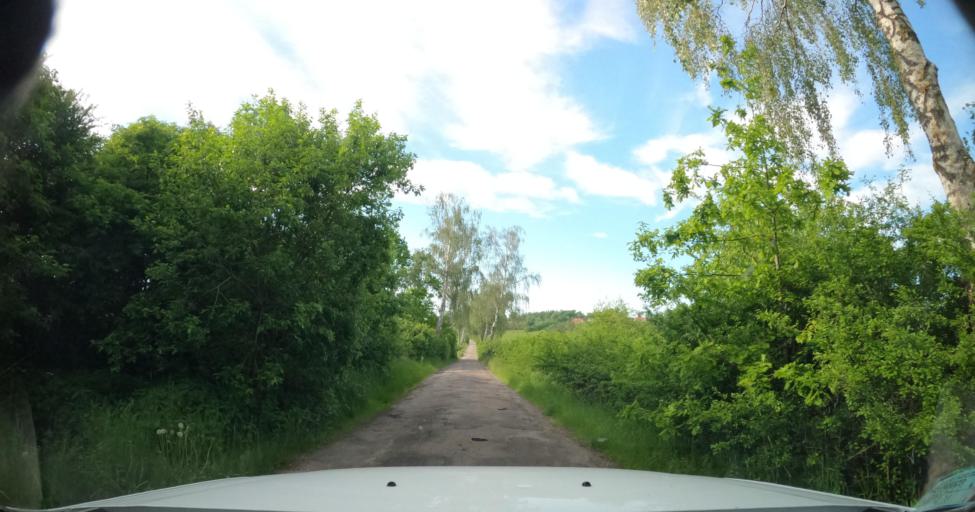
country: PL
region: Warmian-Masurian Voivodeship
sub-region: Powiat ostrodzki
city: Morag
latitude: 54.0561
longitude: 19.8891
